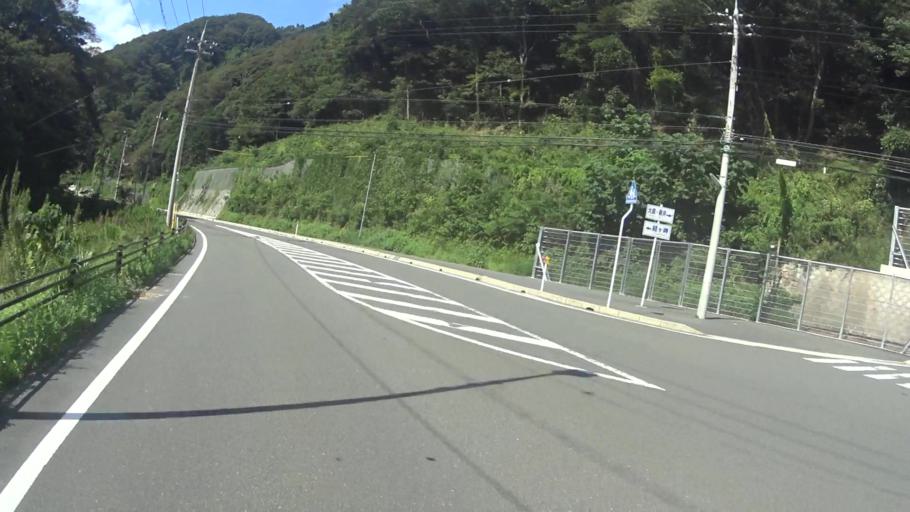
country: JP
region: Kyoto
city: Miyazu
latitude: 35.6861
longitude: 135.2897
